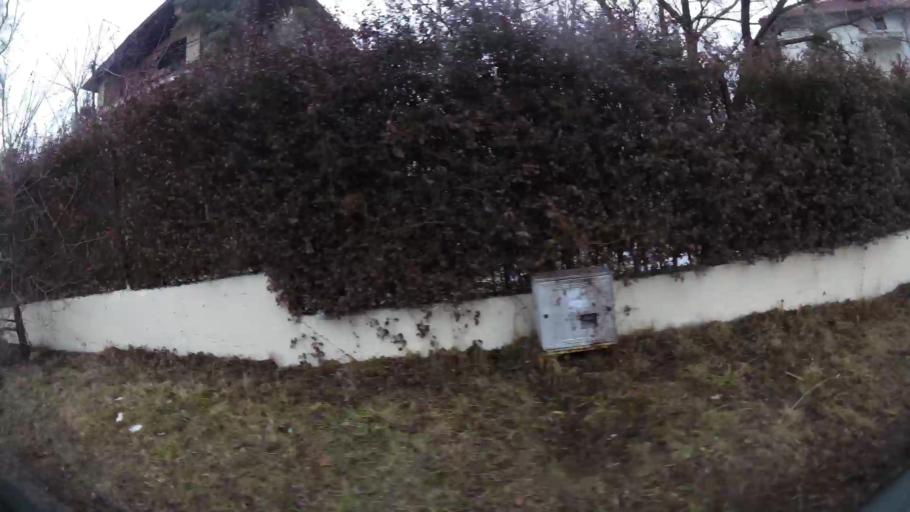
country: BG
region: Sofiya
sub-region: Obshtina Bozhurishte
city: Bozhurishte
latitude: 42.6721
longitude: 23.2384
